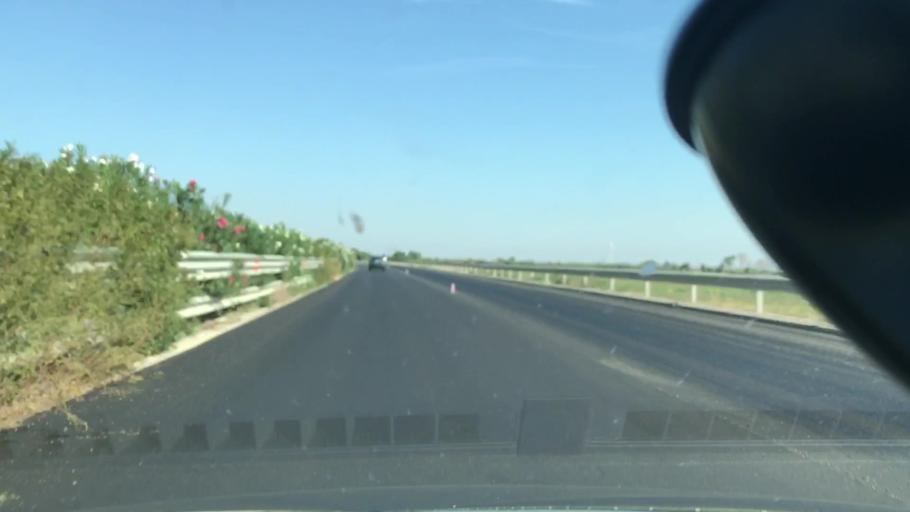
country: IT
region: Apulia
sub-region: Provincia di Foggia
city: Ascoli Satriano
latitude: 41.2773
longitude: 15.5537
